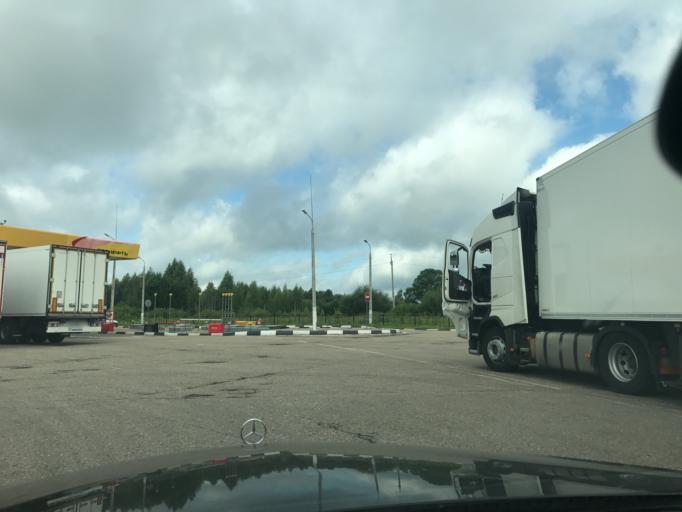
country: RU
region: Smolensk
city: Golynki
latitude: 54.7638
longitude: 31.5153
